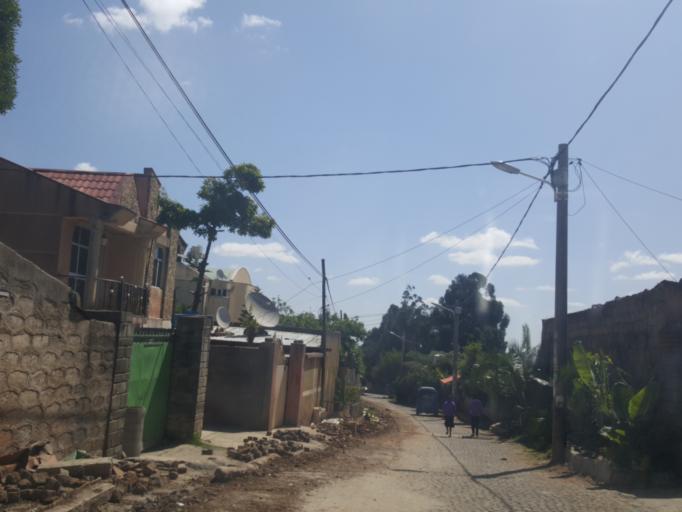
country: ET
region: Adis Abeba
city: Addis Ababa
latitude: 9.0554
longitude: 38.7352
